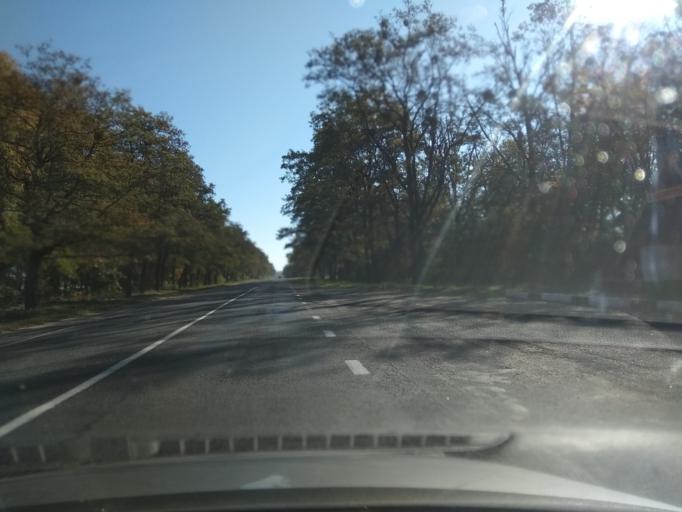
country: BY
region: Brest
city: Malaryta
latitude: 51.9333
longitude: 24.0535
